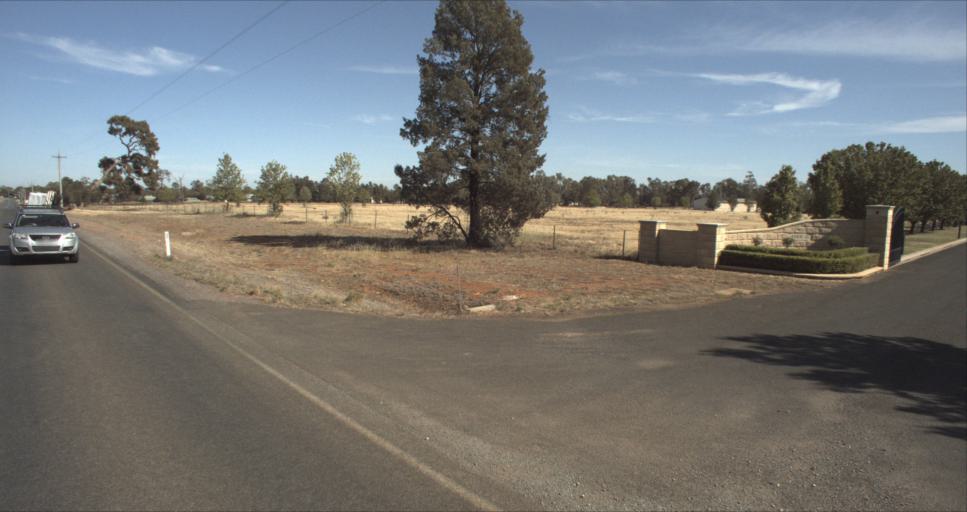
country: AU
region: New South Wales
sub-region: Leeton
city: Leeton
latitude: -34.5645
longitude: 146.4231
